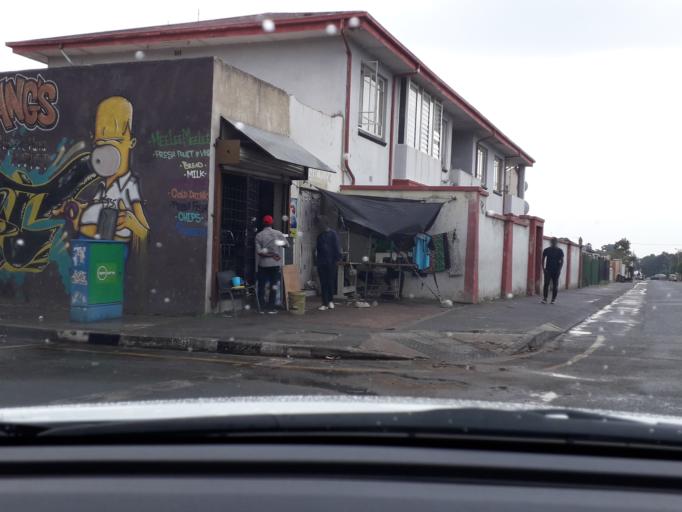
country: ZA
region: Gauteng
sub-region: City of Johannesburg Metropolitan Municipality
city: Johannesburg
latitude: -26.2404
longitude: 28.0552
